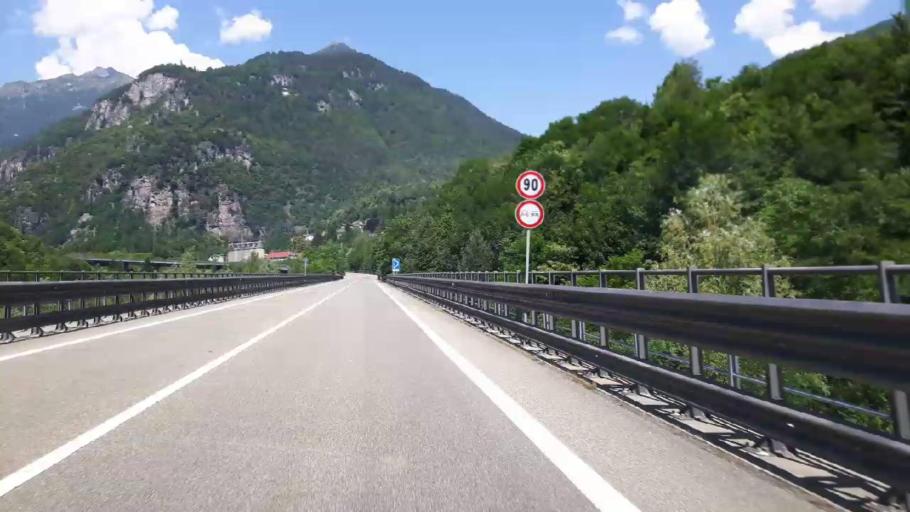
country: IT
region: Piedmont
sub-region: Provincia Verbano-Cusio-Ossola
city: Varzo
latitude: 46.2041
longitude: 8.2487
